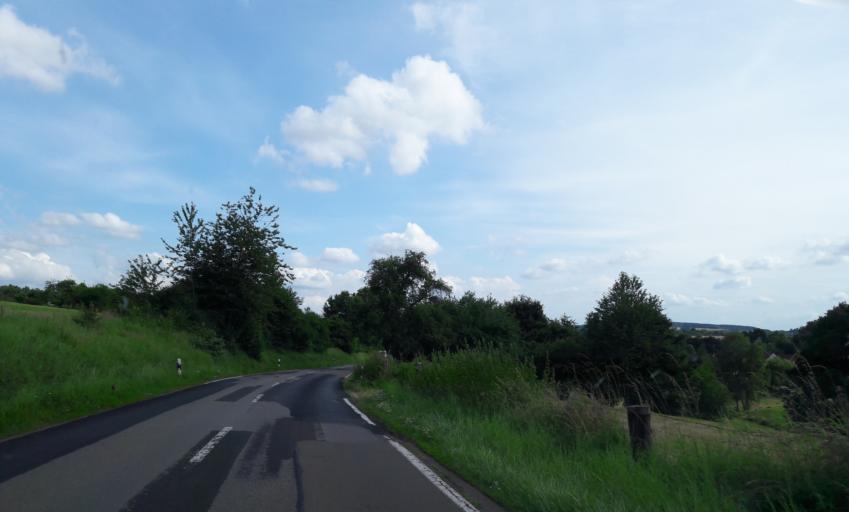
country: DE
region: Saarland
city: Mainzweiler
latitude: 49.4450
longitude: 7.1224
